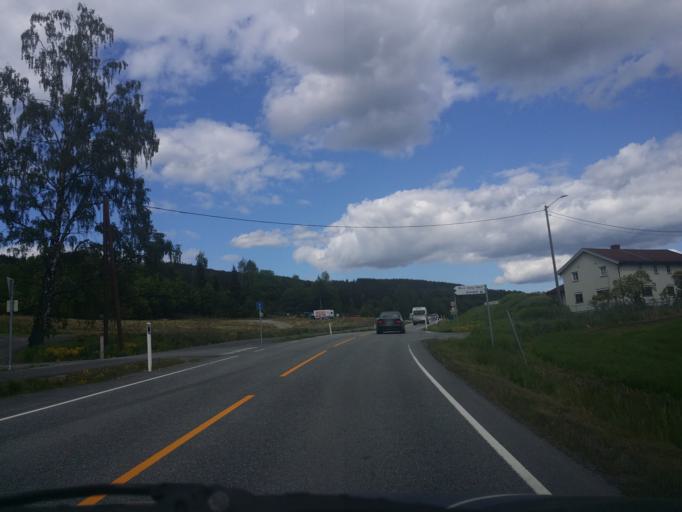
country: NO
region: Oppland
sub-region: Jevnaker
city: Jevnaker
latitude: 60.2573
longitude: 10.4348
